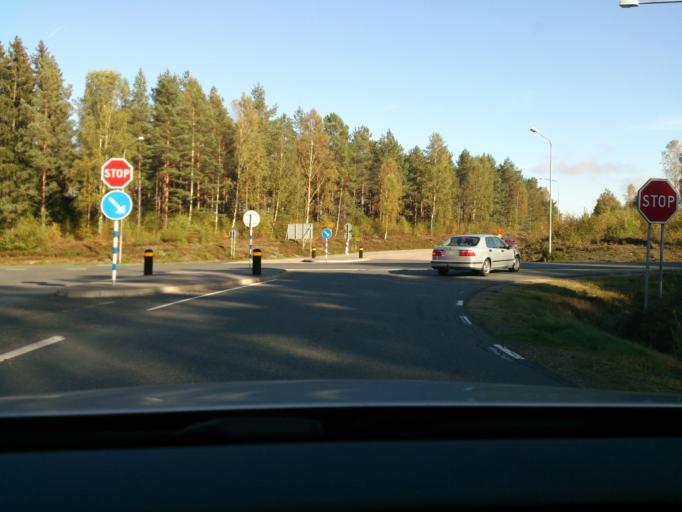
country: SE
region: Kronoberg
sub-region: Alvesta Kommun
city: Moheda
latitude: 57.0001
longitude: 14.5585
